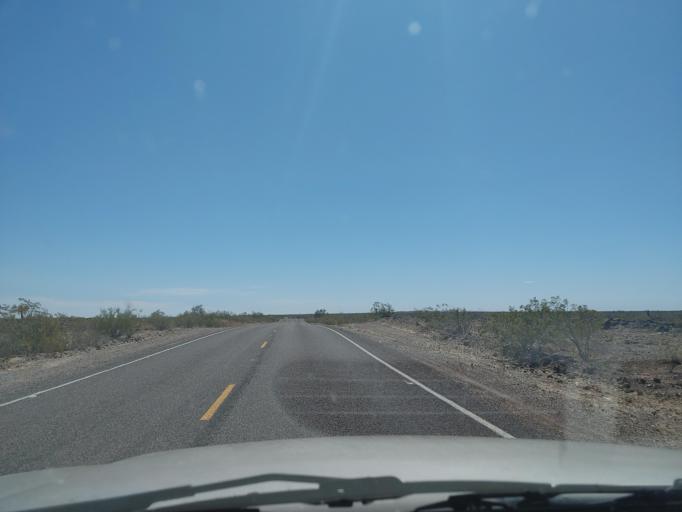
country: US
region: Arizona
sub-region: Maricopa County
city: Gila Bend
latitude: 32.9204
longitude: -113.2852
